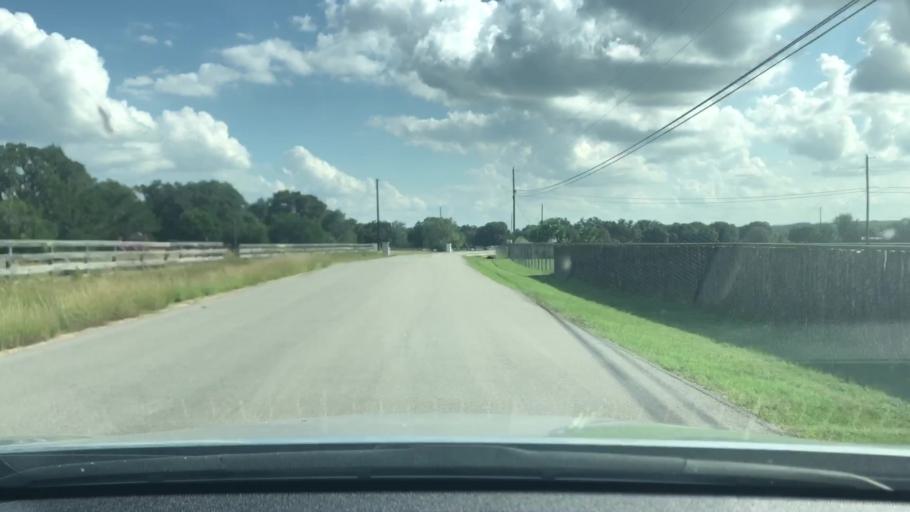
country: US
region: Texas
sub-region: Bexar County
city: Fair Oaks Ranch
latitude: 29.7666
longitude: -98.6311
